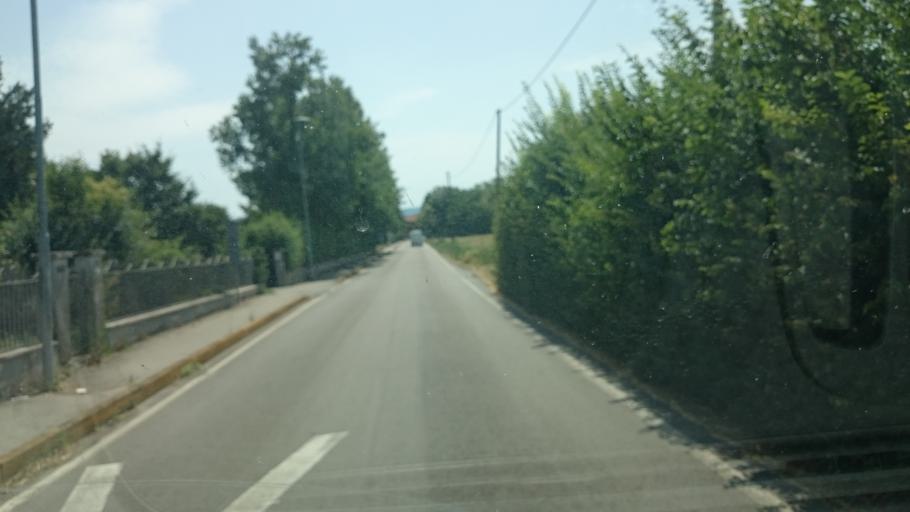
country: IT
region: Emilia-Romagna
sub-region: Provincia di Reggio Emilia
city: Fogliano
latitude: 44.6339
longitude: 10.6663
